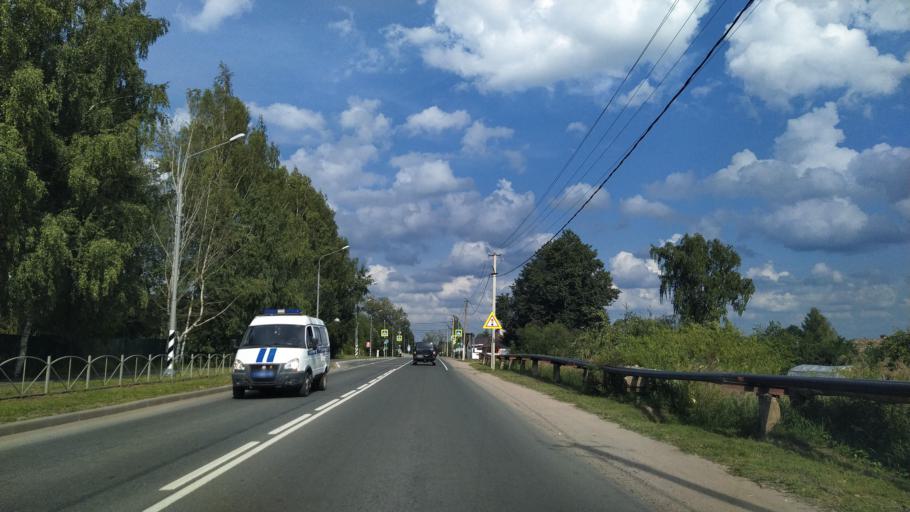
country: RU
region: Novgorod
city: Sol'tsy
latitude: 58.1257
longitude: 30.3452
